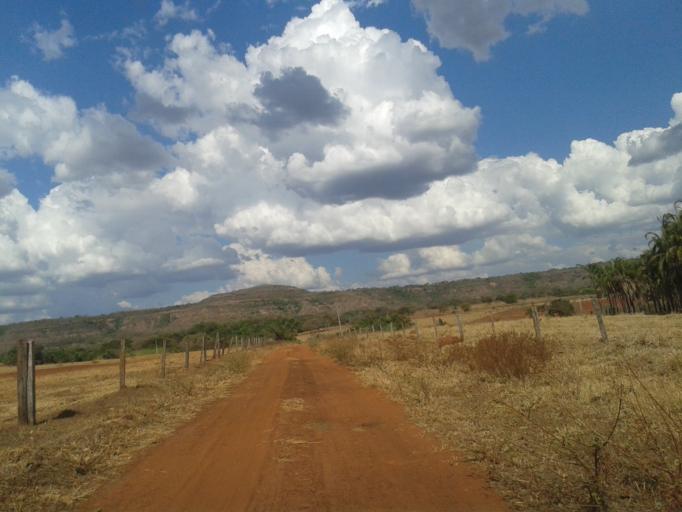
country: BR
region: Minas Gerais
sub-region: Santa Vitoria
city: Santa Vitoria
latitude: -19.2080
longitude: -49.9678
